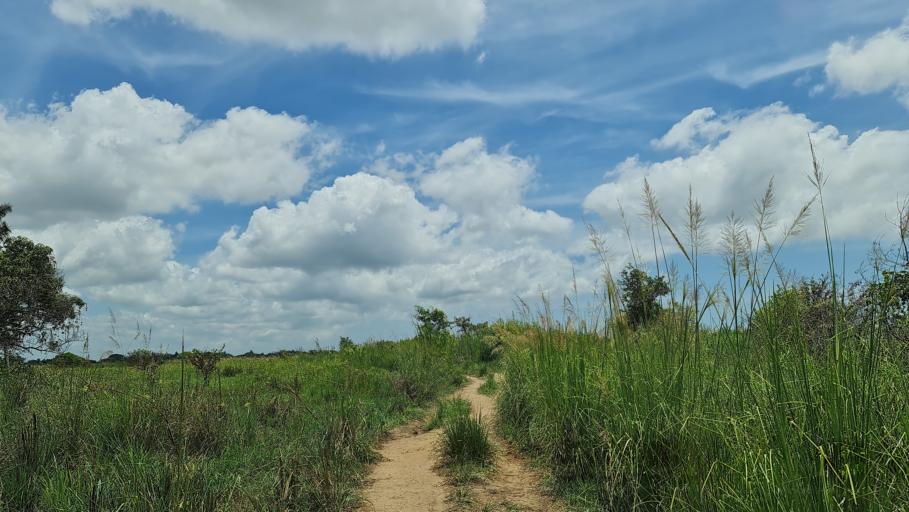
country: MZ
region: Zambezia
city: Quelimane
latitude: -17.5838
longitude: 37.3831
